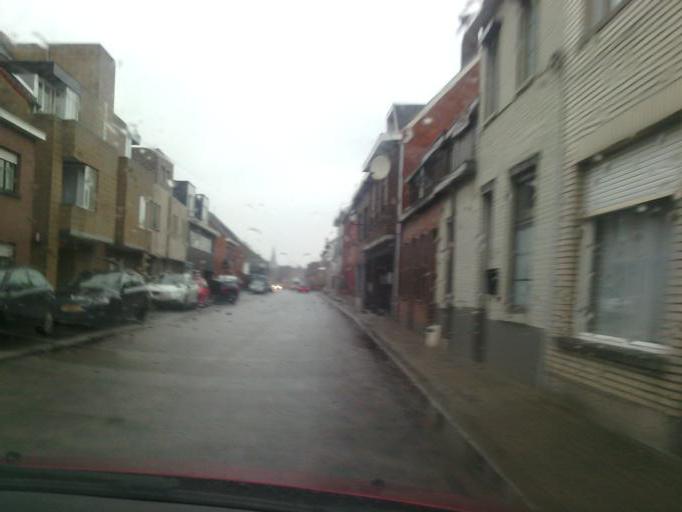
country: BE
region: Flanders
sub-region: Provincie Oost-Vlaanderen
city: Wichelen
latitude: 51.0102
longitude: 3.9335
